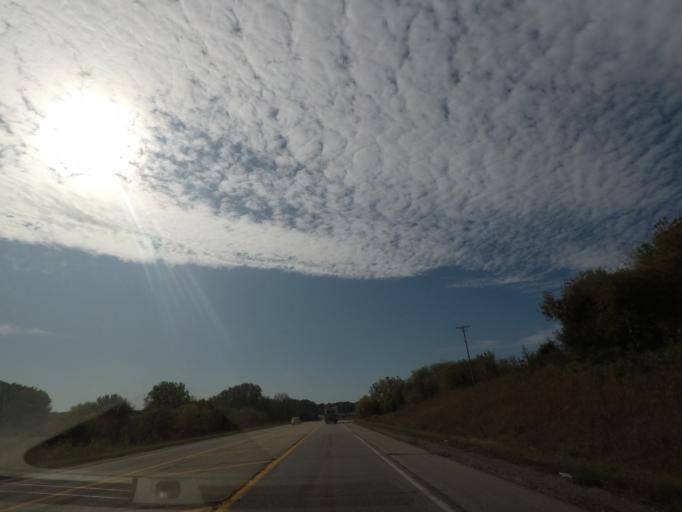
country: US
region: Iowa
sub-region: Story County
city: Ames
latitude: 42.0738
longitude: -93.6216
